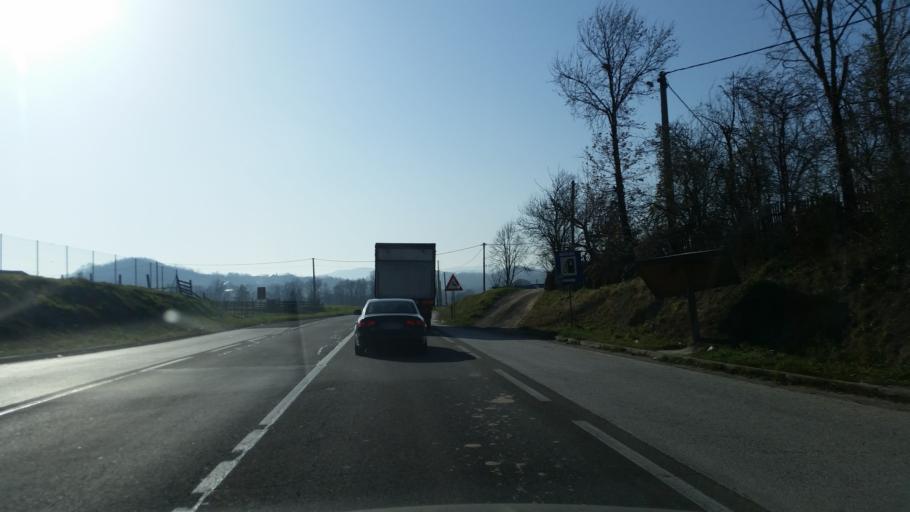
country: RS
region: Central Serbia
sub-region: Kolubarski Okrug
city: Ljig
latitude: 44.2511
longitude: 20.2851
